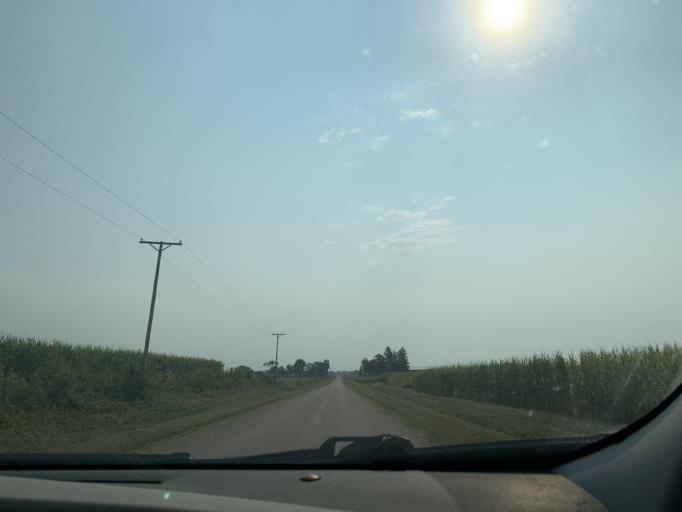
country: US
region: Illinois
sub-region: Whiteside County
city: Morrison
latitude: 41.8697
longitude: -89.9117
